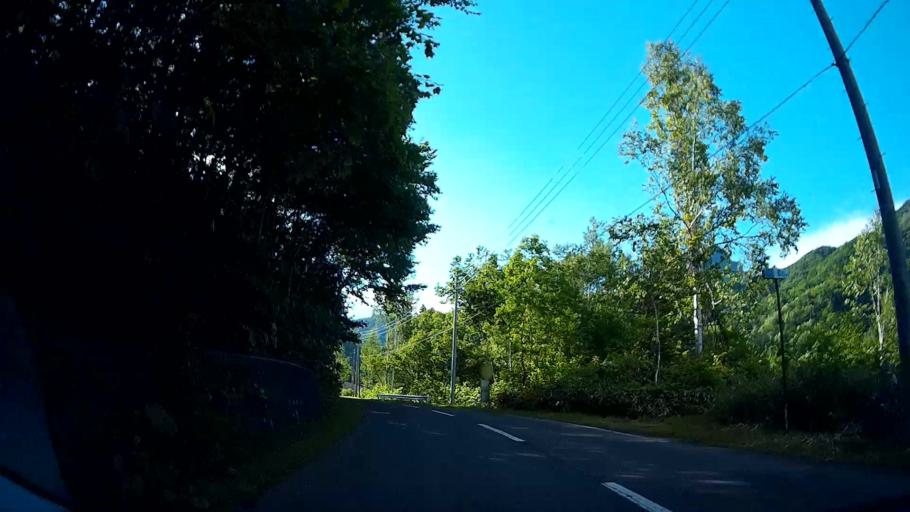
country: JP
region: Hokkaido
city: Otaru
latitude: 42.9883
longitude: 141.1165
